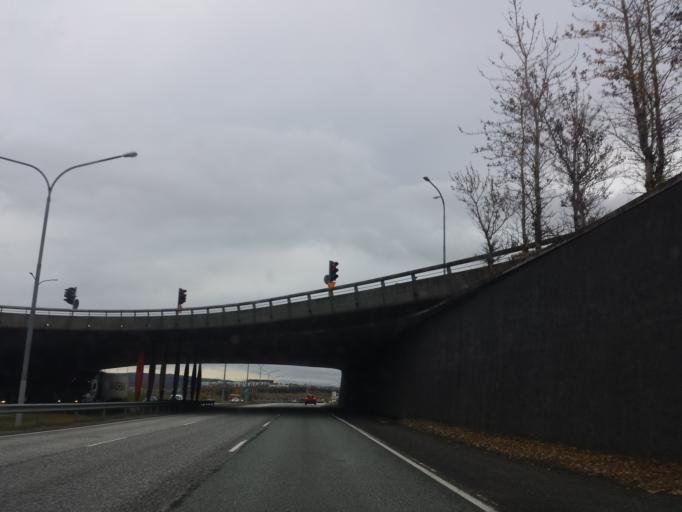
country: IS
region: Capital Region
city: Reykjavik
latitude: 64.1240
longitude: -21.8131
